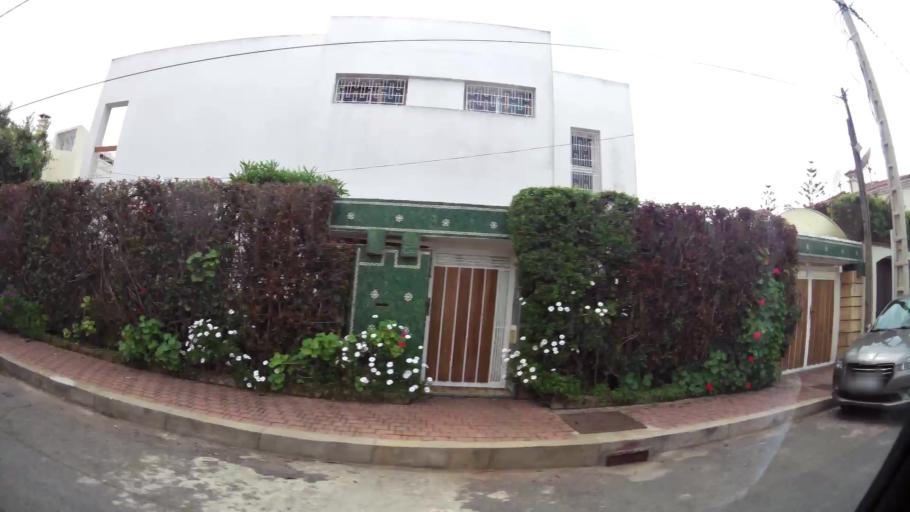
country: MA
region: Grand Casablanca
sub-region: Casablanca
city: Casablanca
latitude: 33.5736
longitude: -7.6606
